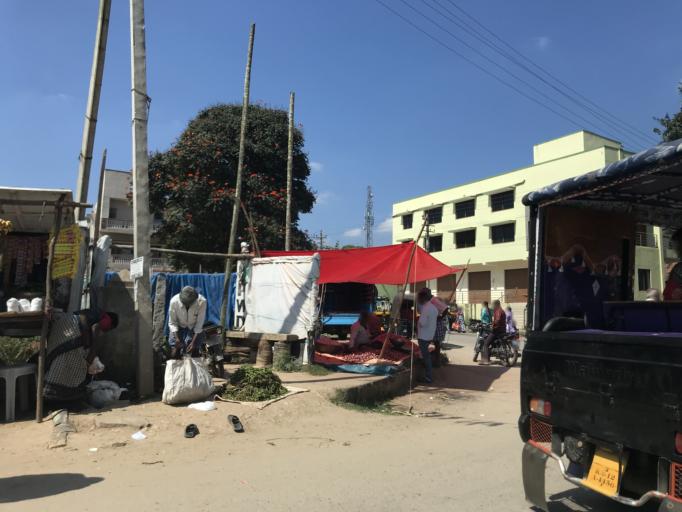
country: IN
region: Karnataka
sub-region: Mysore
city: Heggadadevankote
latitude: 12.0870
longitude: 76.3317
